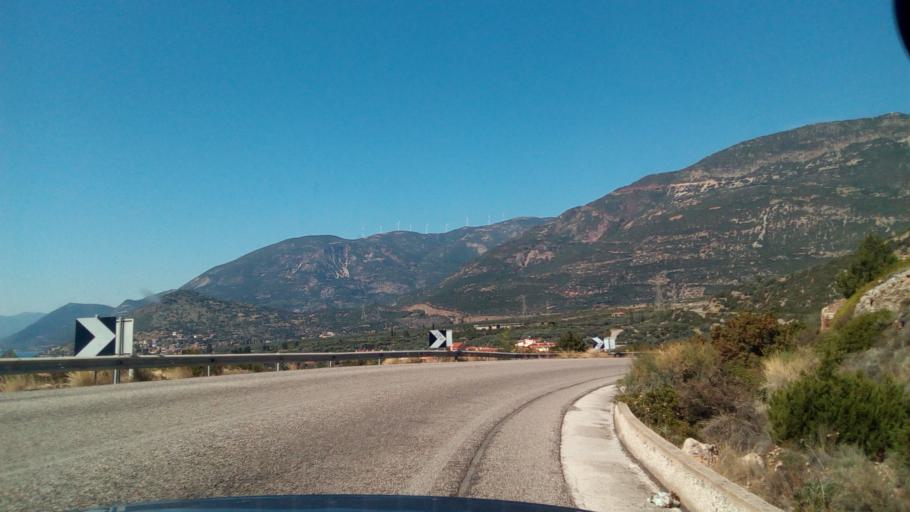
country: GR
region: West Greece
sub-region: Nomos Achaias
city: Selianitika
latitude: 38.3713
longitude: 22.0975
